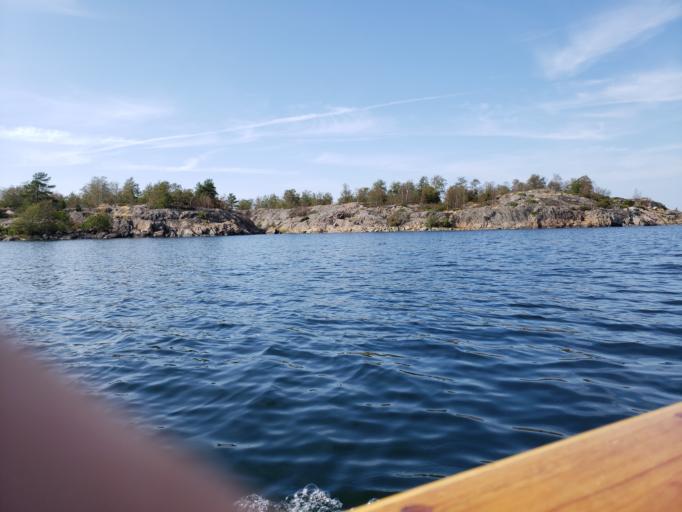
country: FI
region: Varsinais-Suomi
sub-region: Aboland-Turunmaa
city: Dragsfjaerd
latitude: 59.8513
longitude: 22.2131
